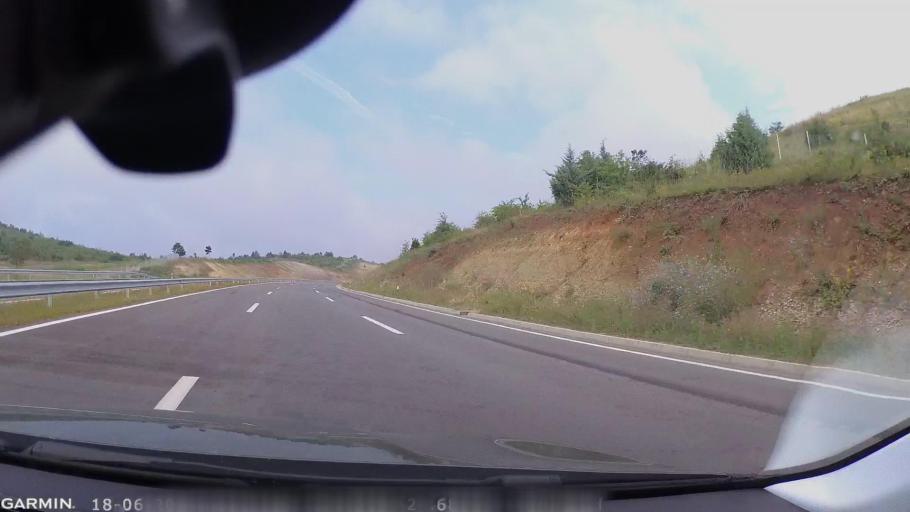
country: MK
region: Petrovec
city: Sredno Konjare
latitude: 41.9450
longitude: 21.7837
